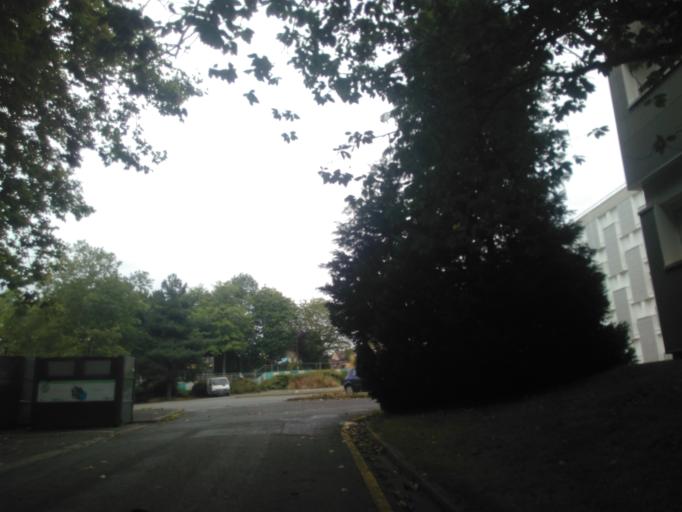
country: FR
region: Brittany
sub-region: Departement d'Ille-et-Vilaine
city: Cesson-Sevigne
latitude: 48.1230
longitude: -1.6349
